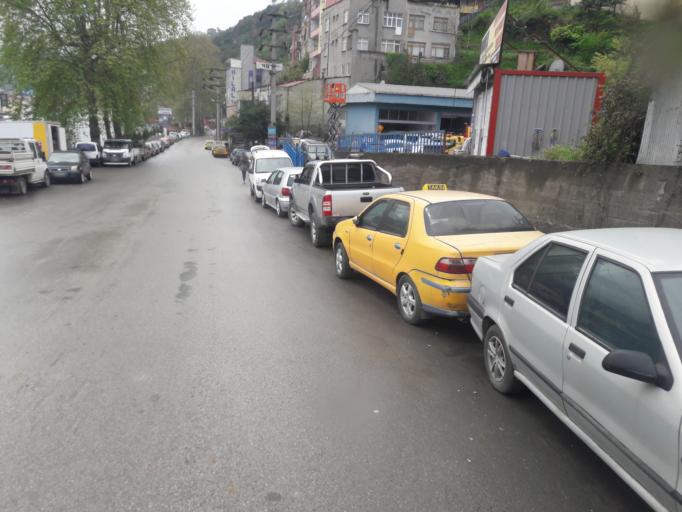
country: TR
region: Trabzon
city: Trabzon
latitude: 40.9924
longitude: 39.7490
